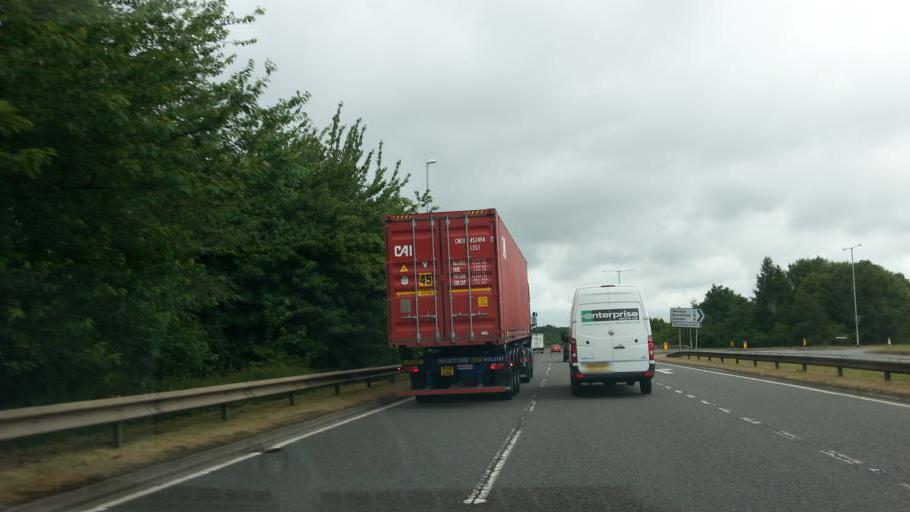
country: GB
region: England
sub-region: Northamptonshire
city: Corby
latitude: 52.4849
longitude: -0.6566
